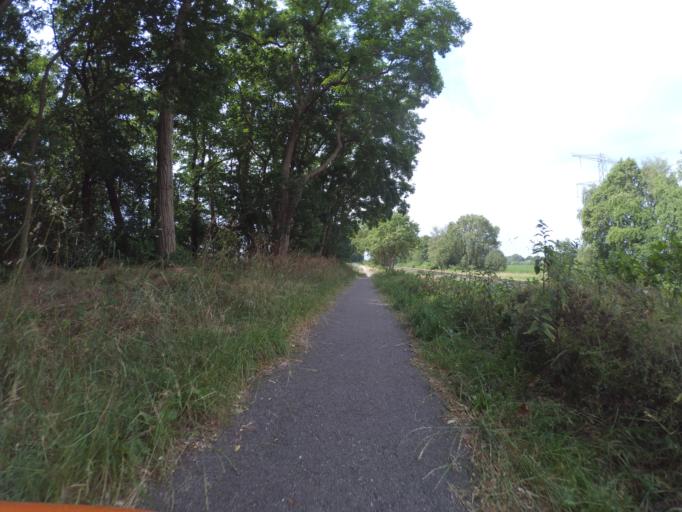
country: NL
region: Overijssel
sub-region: Gemeente Hof van Twente
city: Markelo
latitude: 52.1846
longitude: 6.4794
